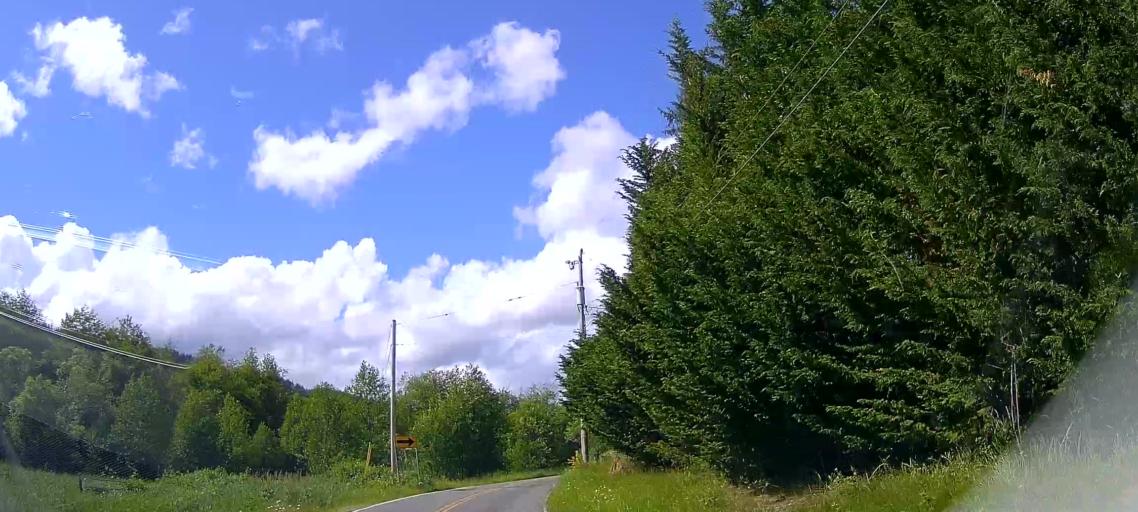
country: US
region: Washington
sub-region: Whatcom County
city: Sudden Valley
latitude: 48.6734
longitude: -122.1965
